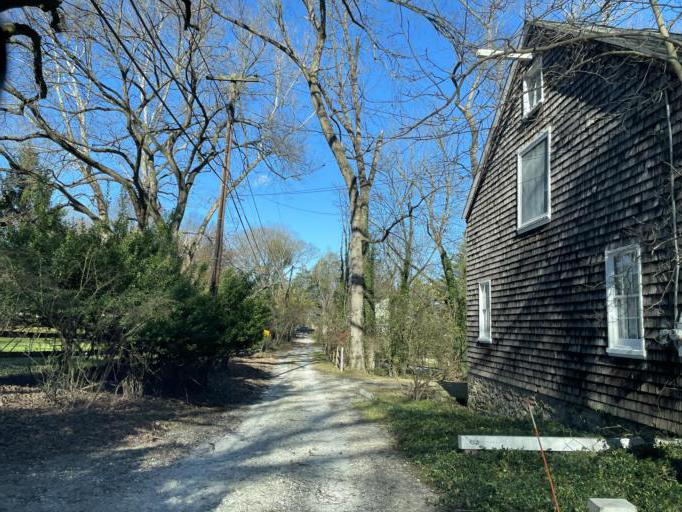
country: US
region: Maryland
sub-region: Baltimore County
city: Mays Chapel
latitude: 39.4078
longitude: -76.6548
